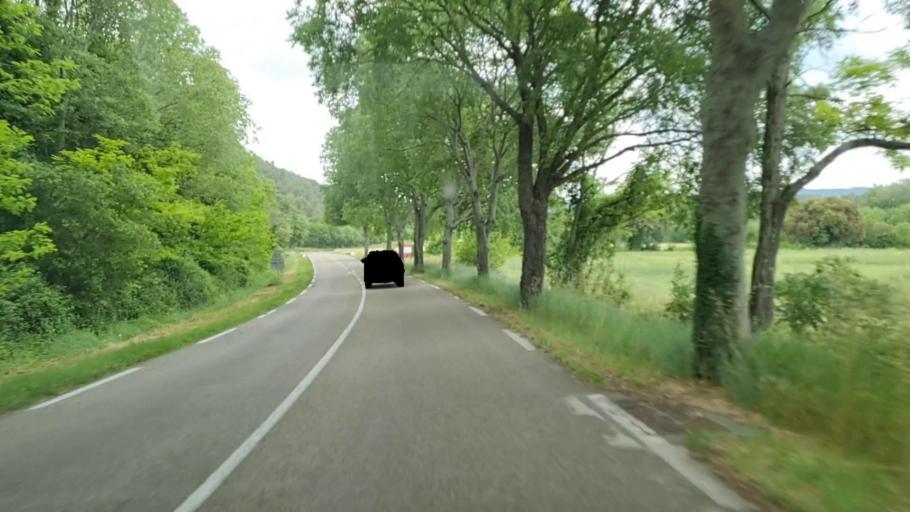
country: FR
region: Languedoc-Roussillon
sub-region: Departement du Gard
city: Quissac
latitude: 43.8772
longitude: 4.0599
